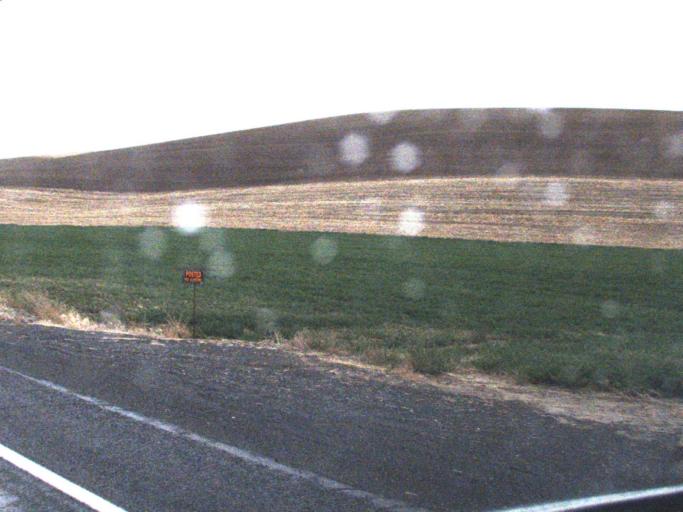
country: US
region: Washington
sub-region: Whitman County
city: Colfax
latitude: 46.8042
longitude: -117.5557
